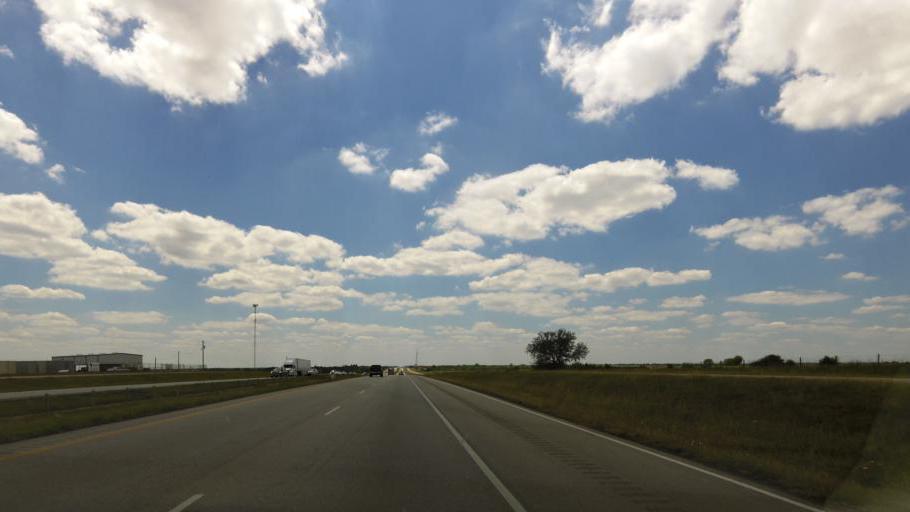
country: US
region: Texas
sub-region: Colorado County
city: Eagle Lake
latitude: 29.7379
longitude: -96.3490
